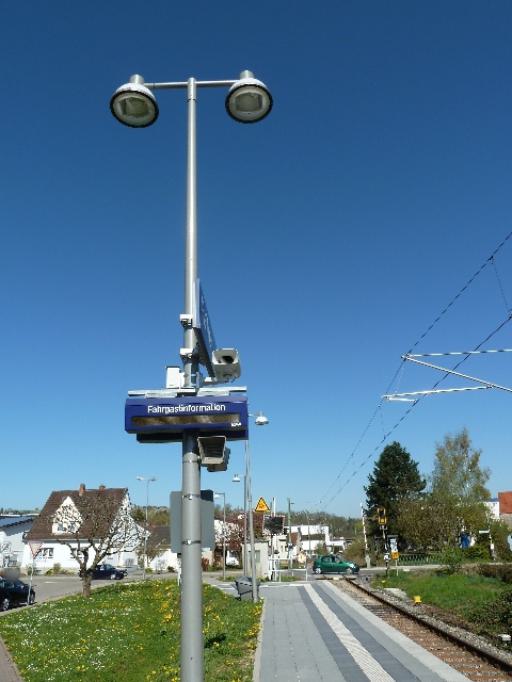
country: DE
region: Baden-Wuerttemberg
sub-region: Regierungsbezirk Stuttgart
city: Ittlingen
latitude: 49.2170
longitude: 8.9199
